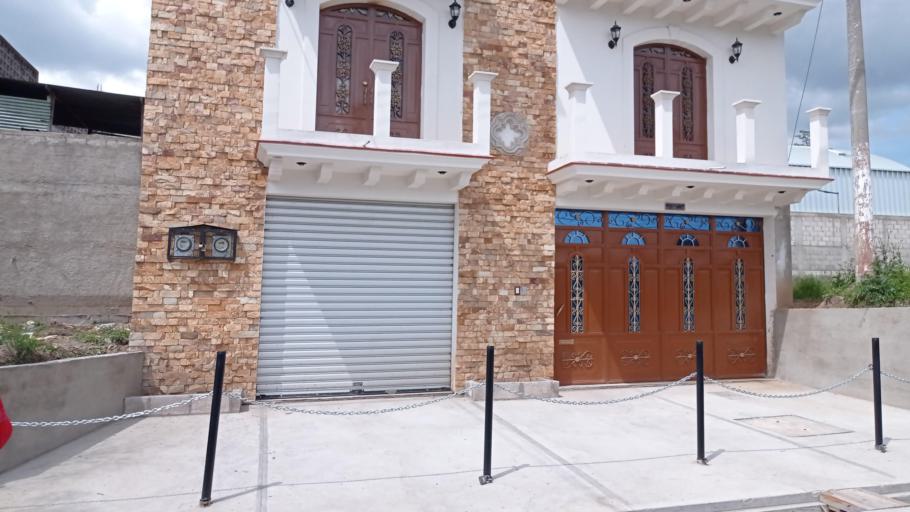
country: GT
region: Quetzaltenango
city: Quetzaltenango
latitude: 14.8527
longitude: -91.4946
